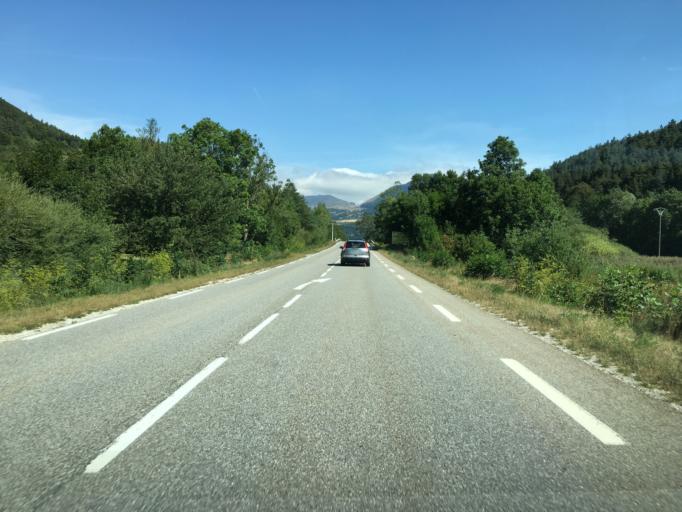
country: FR
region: Rhone-Alpes
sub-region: Departement de l'Isere
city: Mens
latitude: 44.6577
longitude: 5.6941
